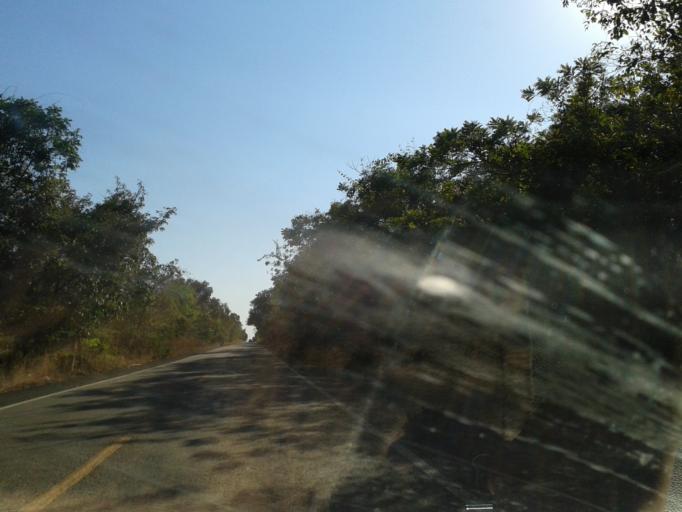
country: BR
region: Goias
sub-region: Mozarlandia
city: Mozarlandia
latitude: -15.0355
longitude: -50.6029
